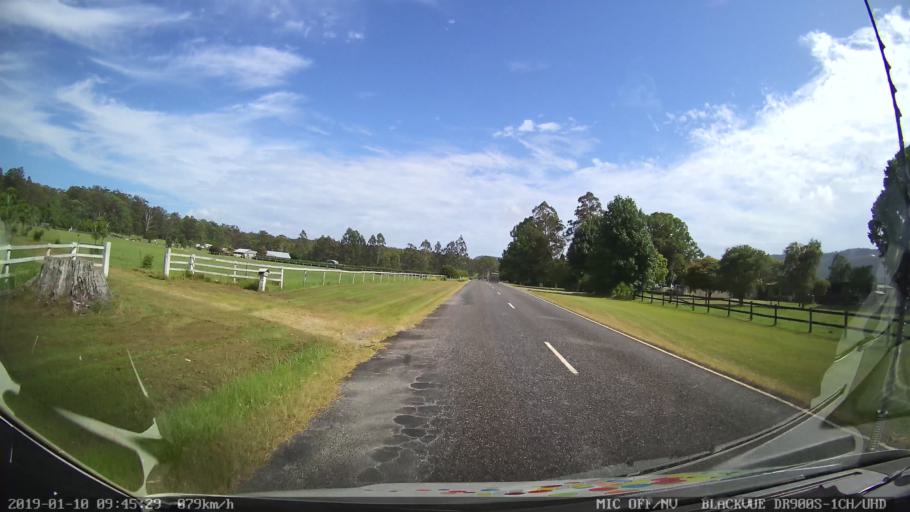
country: AU
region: New South Wales
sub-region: Coffs Harbour
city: Nana Glen
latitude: -30.1041
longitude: 153.0037
